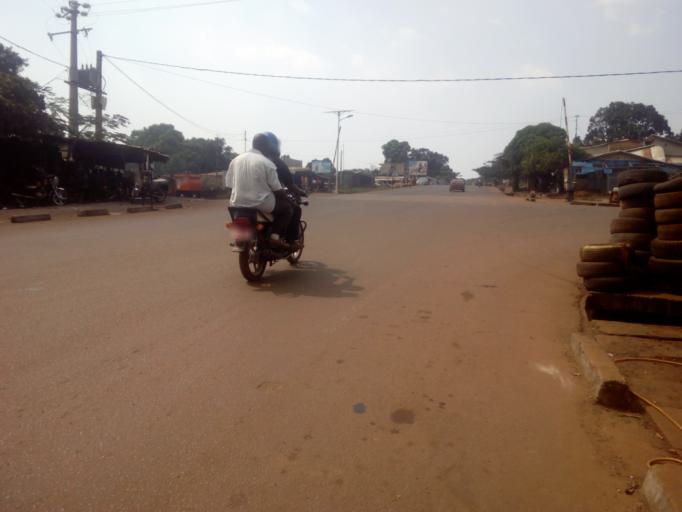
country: GN
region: Conakry
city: Conakry
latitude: 9.6376
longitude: -13.5763
